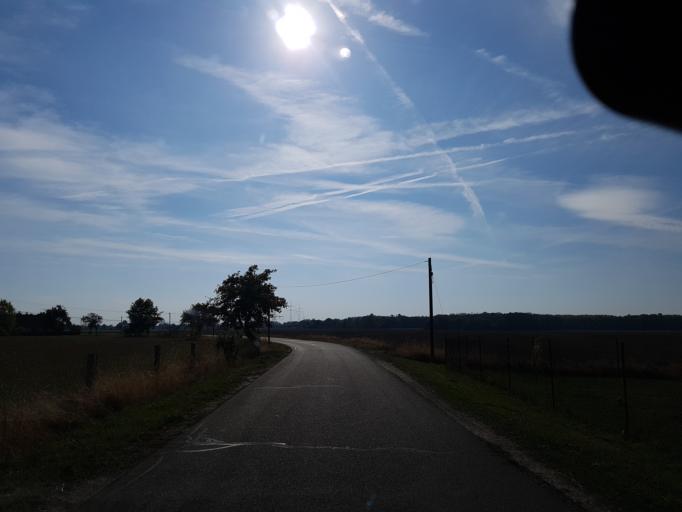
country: DE
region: Brandenburg
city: Doberlug-Kirchhain
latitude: 51.6488
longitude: 13.5446
